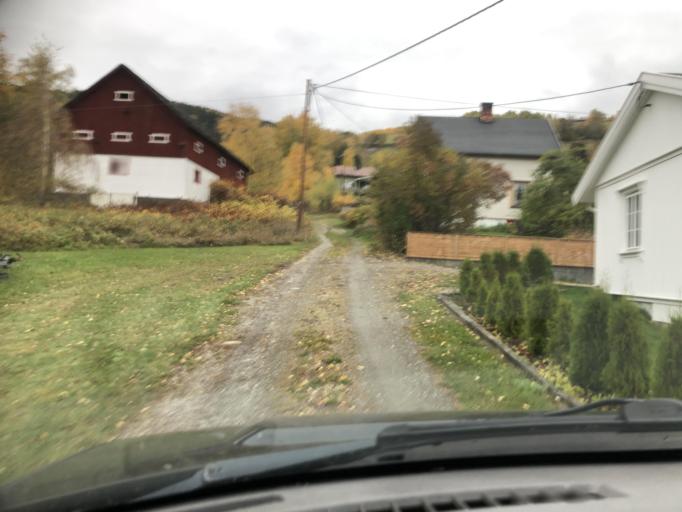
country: NO
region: Oppland
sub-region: Sor-Fron
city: Hundorp
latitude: 61.5747
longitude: 9.9137
